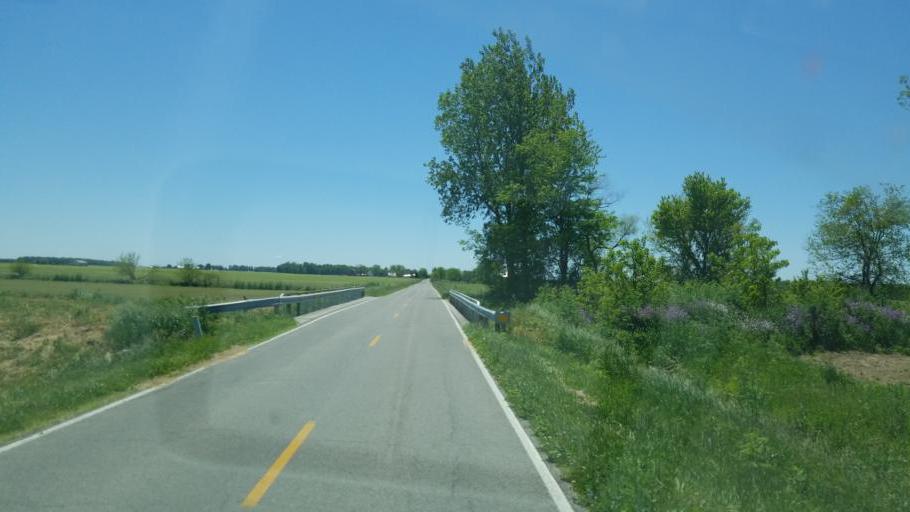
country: US
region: Indiana
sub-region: Randolph County
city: Union City
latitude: 40.2924
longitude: -84.8039
